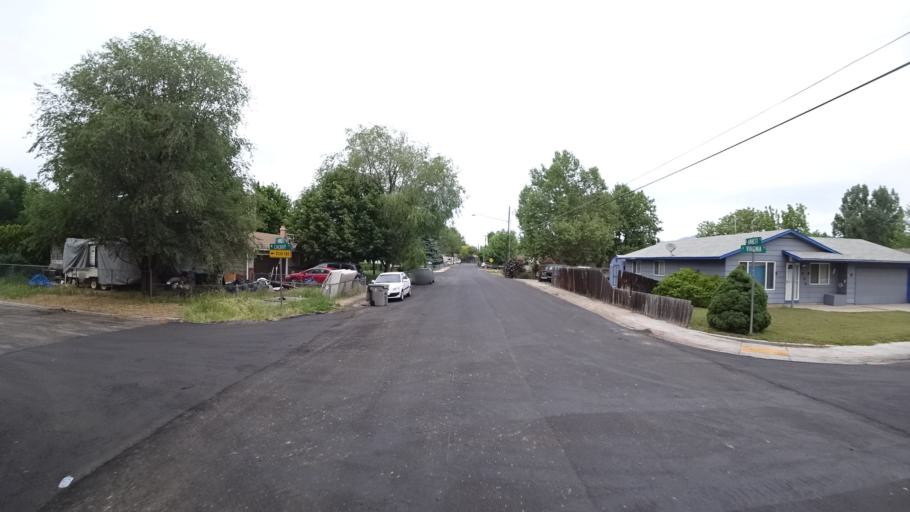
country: US
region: Idaho
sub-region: Ada County
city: Boise
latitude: 43.5808
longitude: -116.2036
